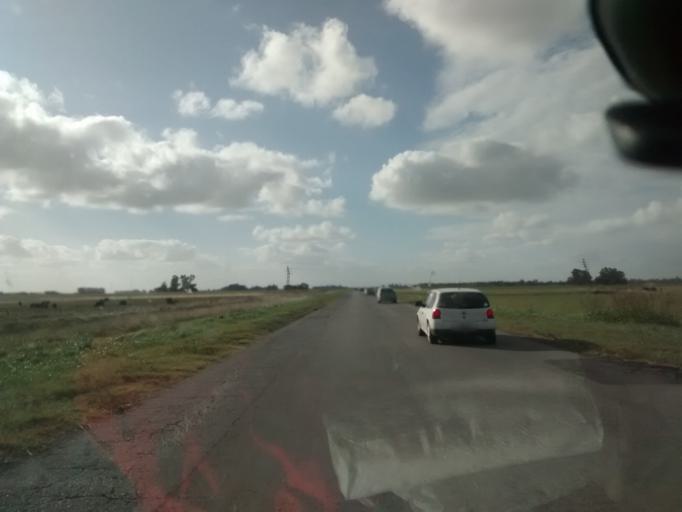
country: AR
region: Buenos Aires
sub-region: Partido de Ayacucho
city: Ayacucho
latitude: -37.1977
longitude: -58.5078
